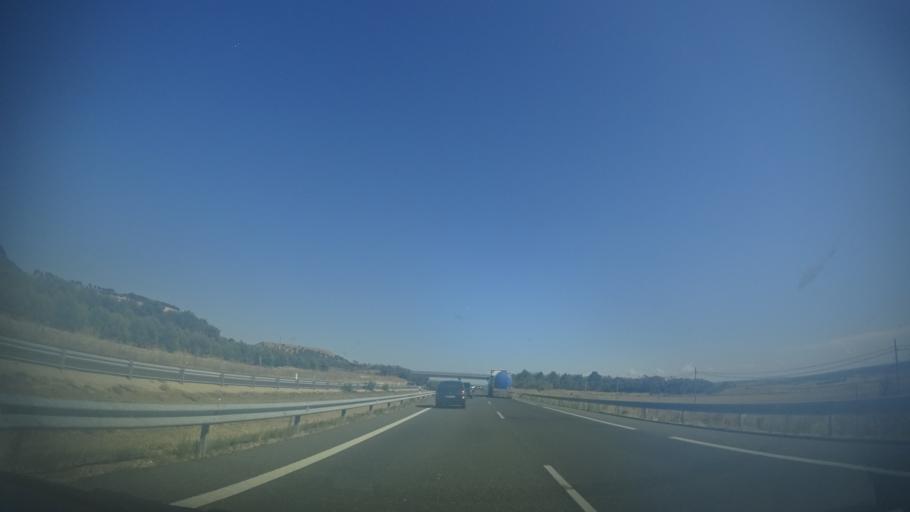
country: ES
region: Castille and Leon
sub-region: Provincia de Valladolid
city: Bercero
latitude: 41.5348
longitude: -5.0619
